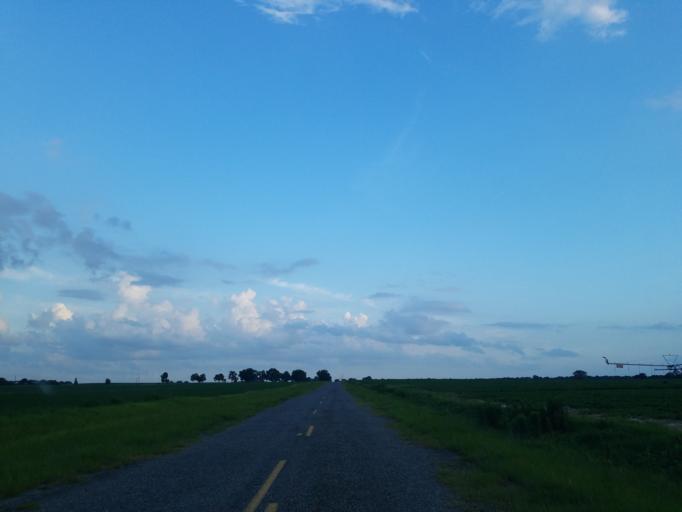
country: US
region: Georgia
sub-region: Dooly County
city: Unadilla
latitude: 32.1719
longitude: -83.7206
